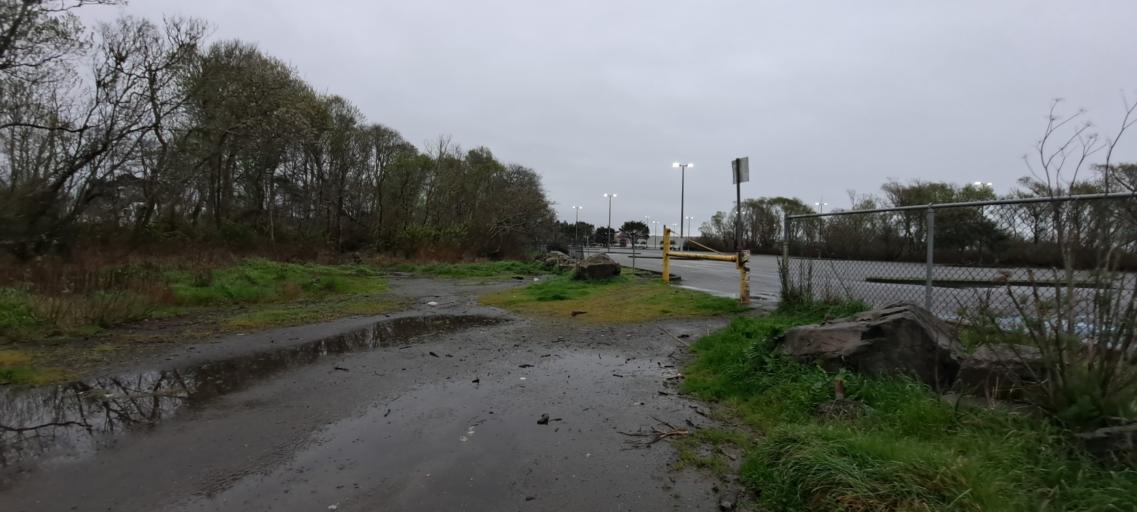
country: US
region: California
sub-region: Humboldt County
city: Bayview
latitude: 40.7845
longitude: -124.1874
